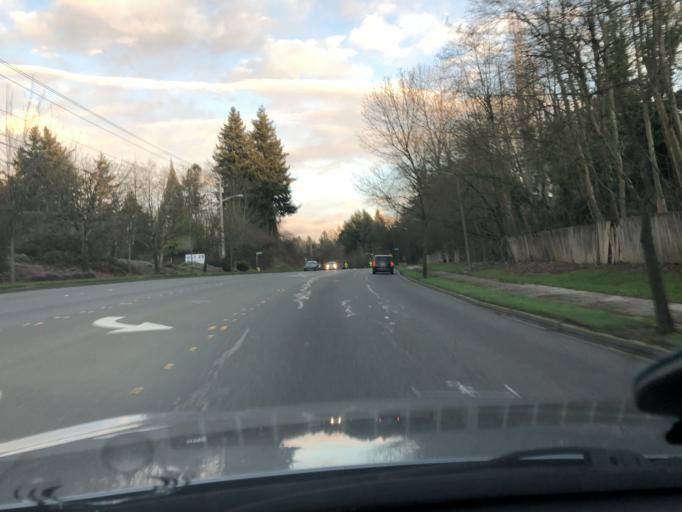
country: US
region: Washington
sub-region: King County
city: Federal Way
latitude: 47.3152
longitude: -122.3450
